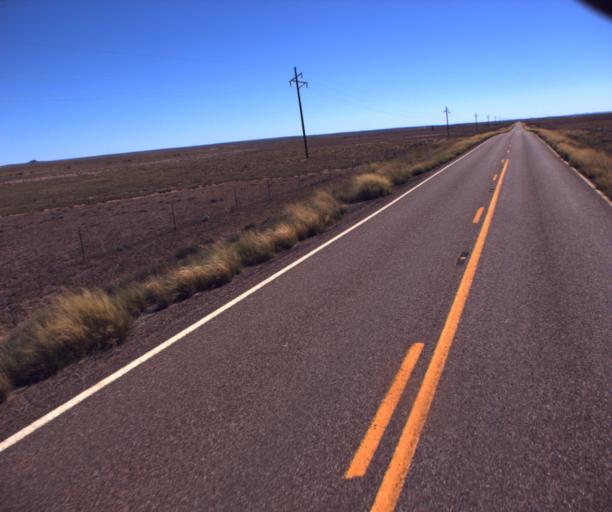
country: US
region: Arizona
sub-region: Navajo County
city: Holbrook
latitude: 35.1170
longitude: -110.0933
